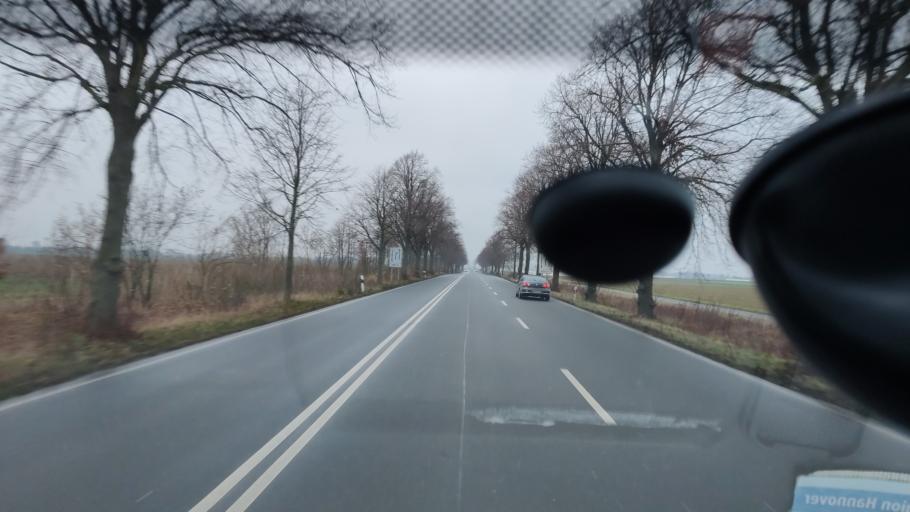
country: DE
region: Lower Saxony
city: Pattensen
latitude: 52.2793
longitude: 9.7587
